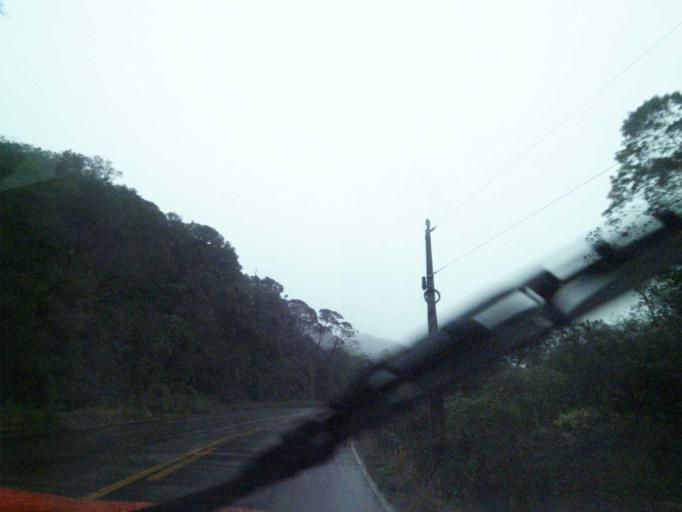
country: BR
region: Santa Catarina
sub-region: Anitapolis
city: Anitapolis
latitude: -27.7542
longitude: -49.0351
